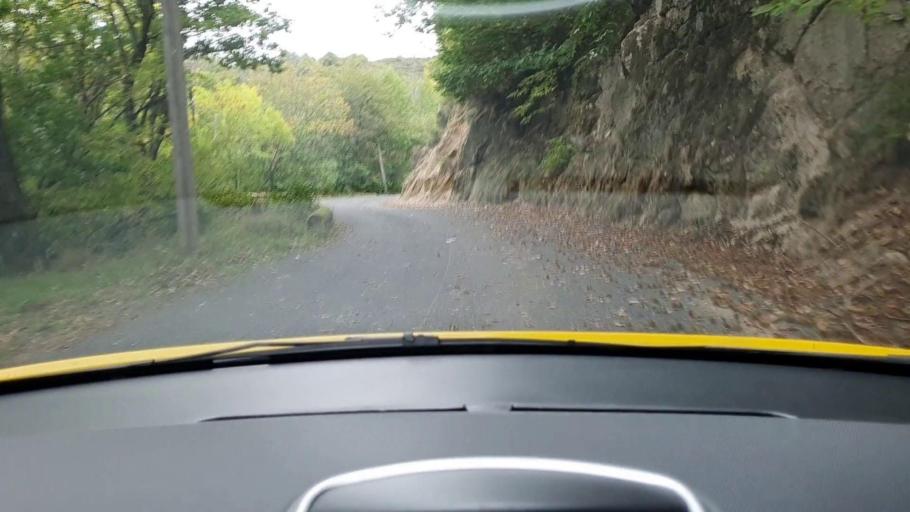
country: FR
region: Languedoc-Roussillon
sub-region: Departement de la Lozere
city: Meyrueis
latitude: 44.0620
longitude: 3.4307
